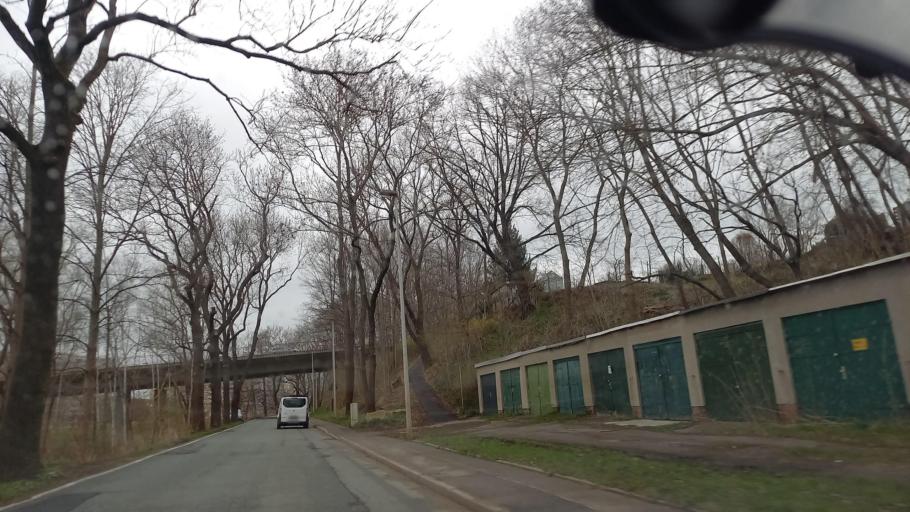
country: DE
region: Saxony
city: Zwickau
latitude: 50.7141
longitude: 12.5027
